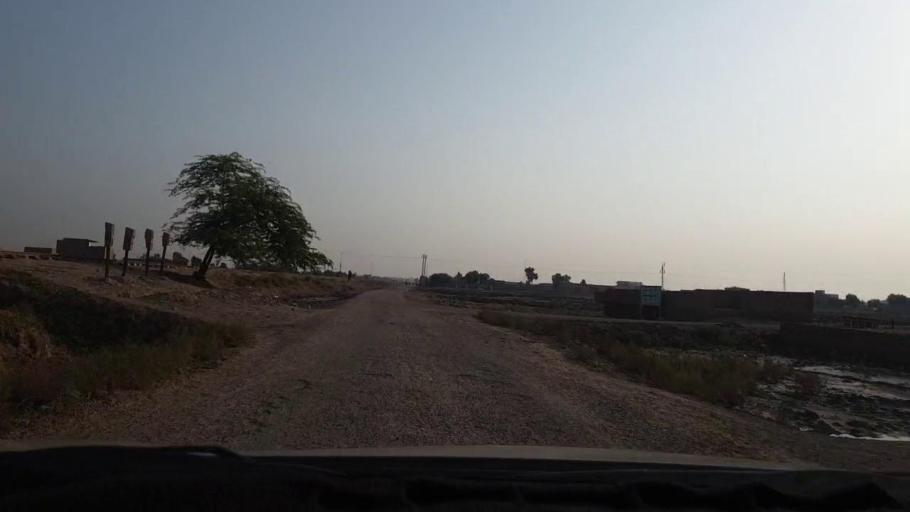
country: PK
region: Sindh
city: Larkana
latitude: 27.5265
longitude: 68.1965
